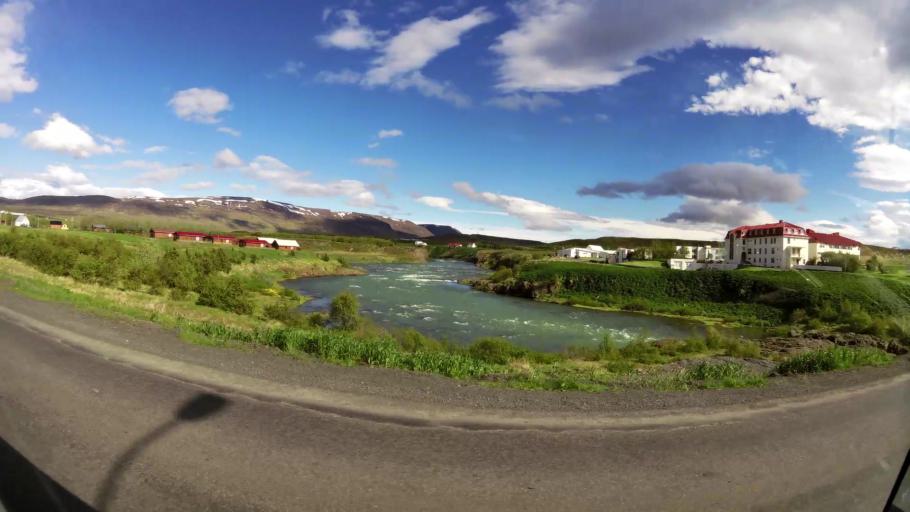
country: IS
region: Northwest
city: Saudarkrokur
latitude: 65.6580
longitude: -20.2816
